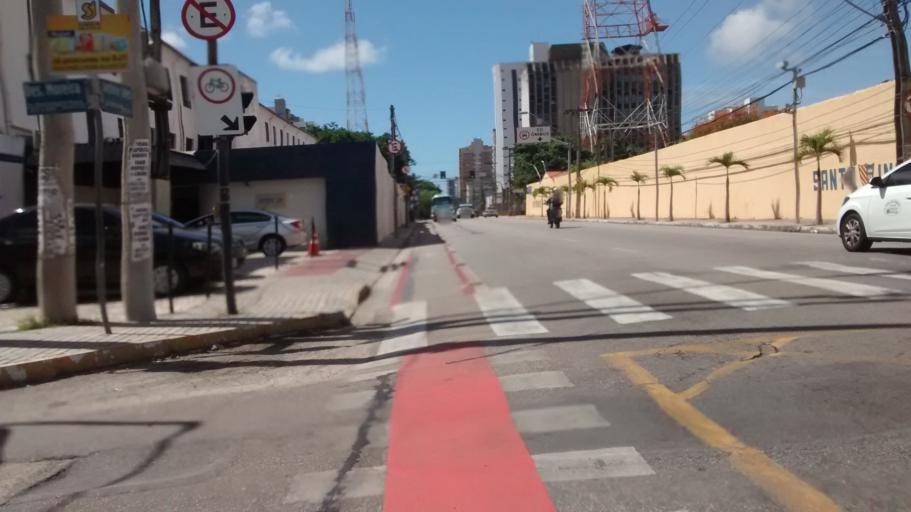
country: BR
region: Ceara
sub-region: Fortaleza
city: Fortaleza
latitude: -3.7457
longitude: -38.5015
